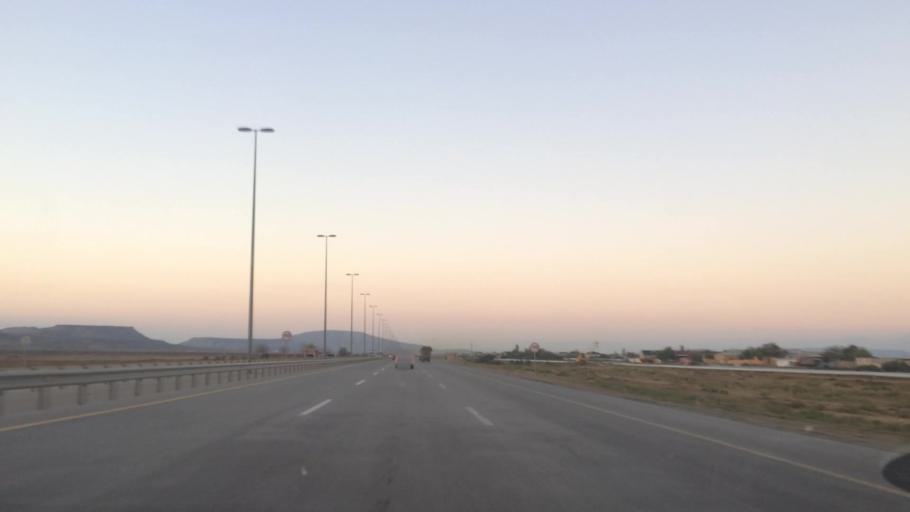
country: AZ
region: Baki
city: Qobustan
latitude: 40.0140
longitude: 49.4266
